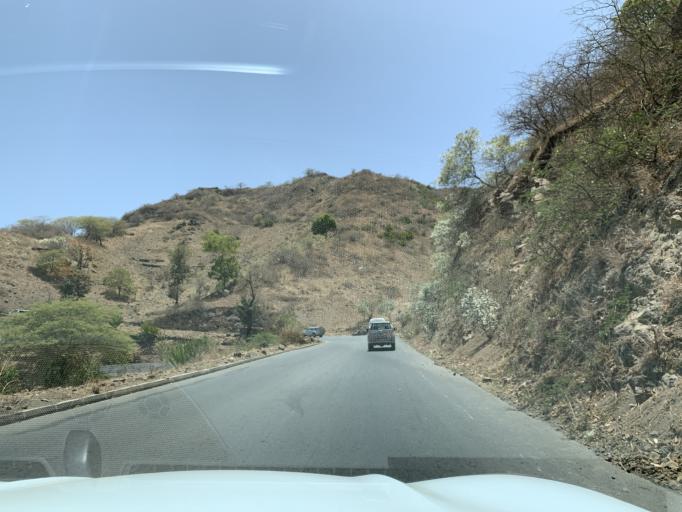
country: CV
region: Sao Salvador do Mundo
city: Picos
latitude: 15.0670
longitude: -23.6175
